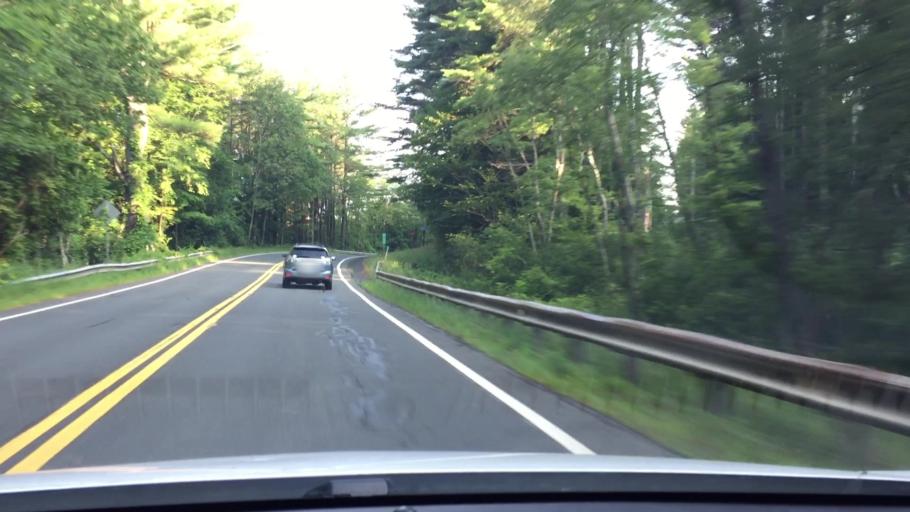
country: US
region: Massachusetts
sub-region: Berkshire County
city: Otis
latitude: 42.2245
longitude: -73.1064
